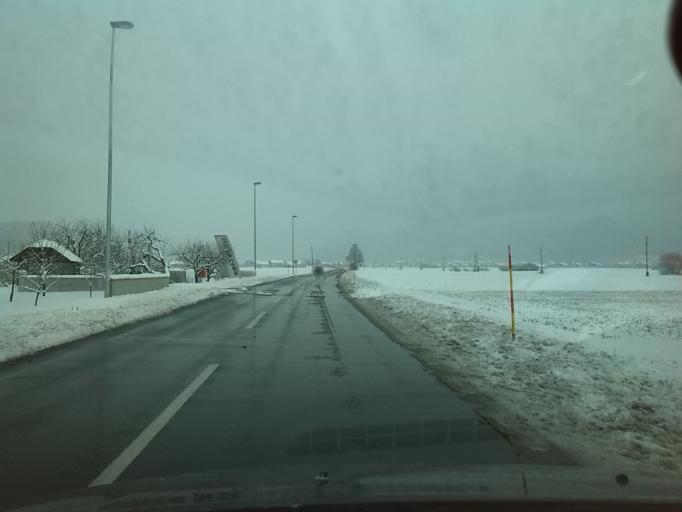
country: SI
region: Kamnik
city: Smarca
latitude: 46.2062
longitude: 14.5808
